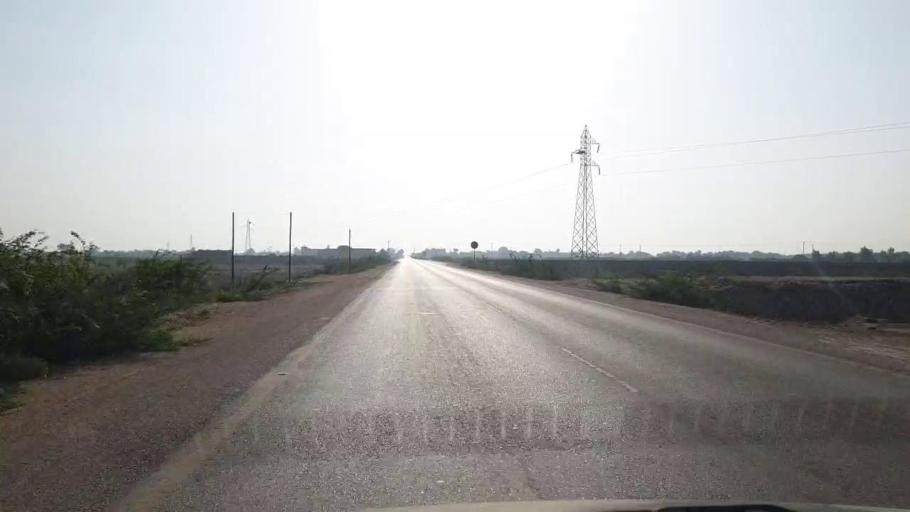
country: PK
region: Sindh
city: Badin
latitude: 24.6794
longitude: 68.8429
